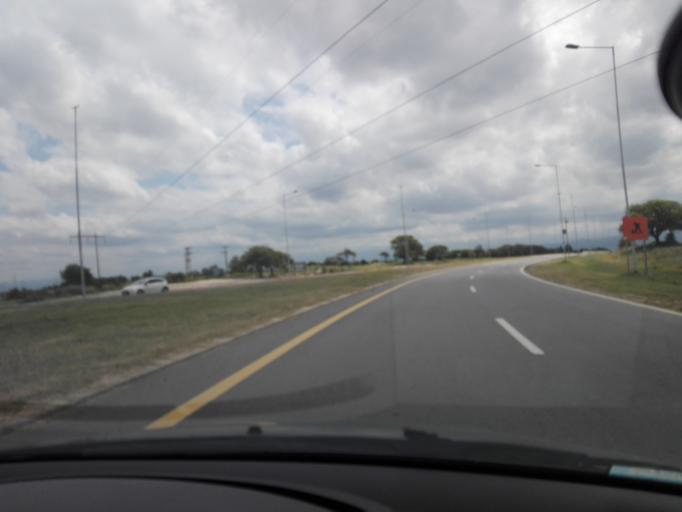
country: AR
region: Cordoba
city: Alta Gracia
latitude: -31.6519
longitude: -64.3163
